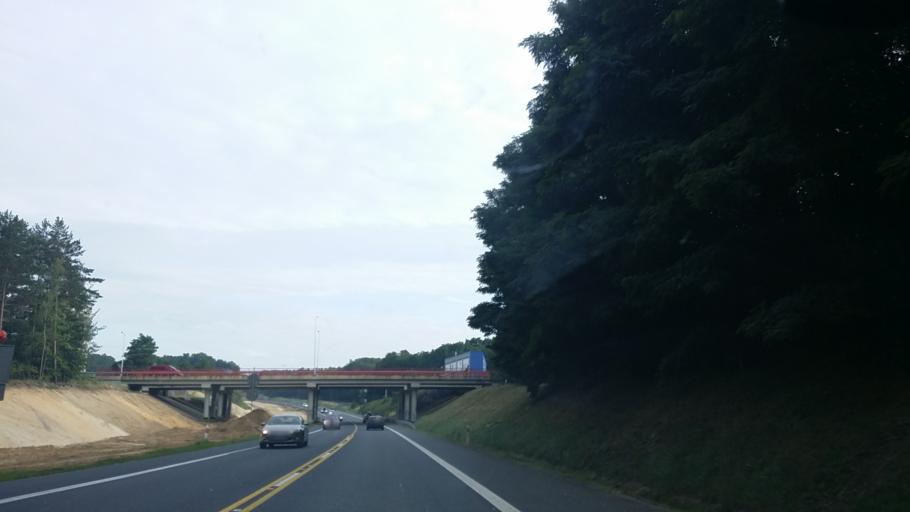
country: PL
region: Lubusz
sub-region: Zielona Gora
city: Zielona Gora
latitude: 51.9397
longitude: 15.5478
